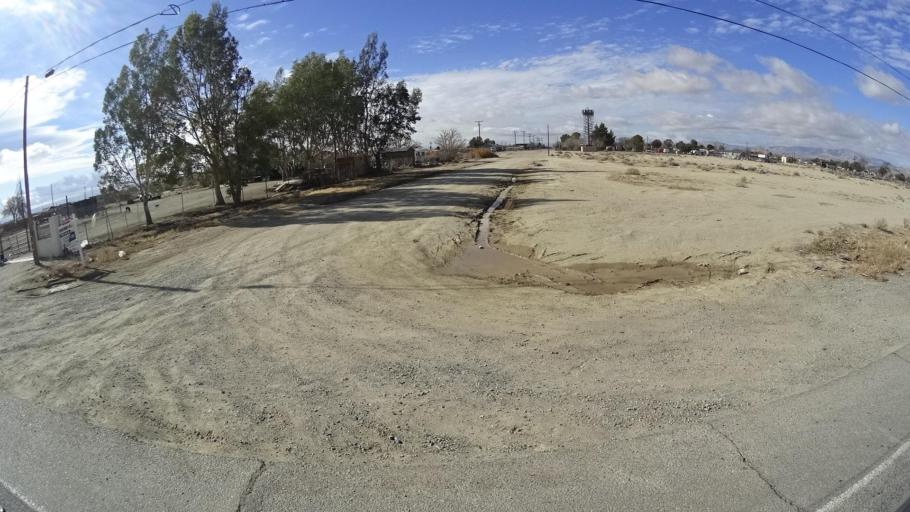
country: US
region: California
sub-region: Kern County
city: Rosamond
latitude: 34.8522
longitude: -118.1608
